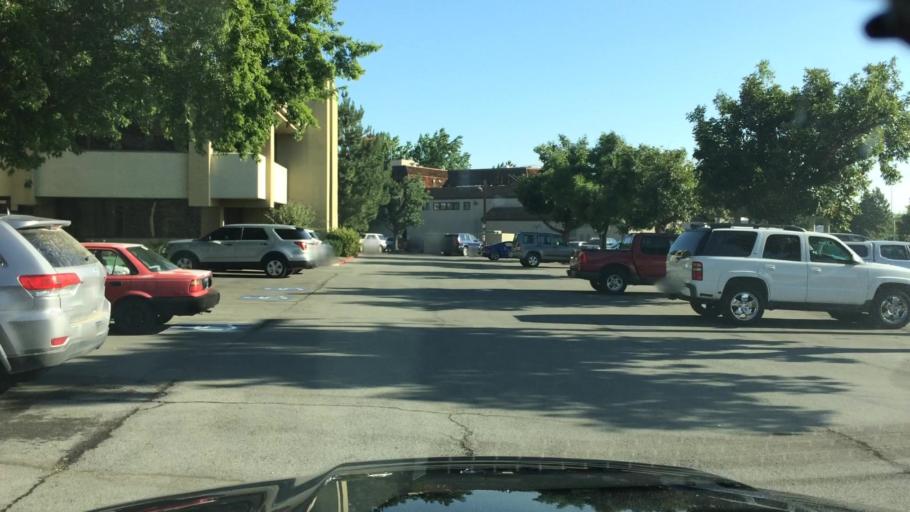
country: US
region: Nevada
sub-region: Washoe County
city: Sparks
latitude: 39.5066
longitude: -119.7787
